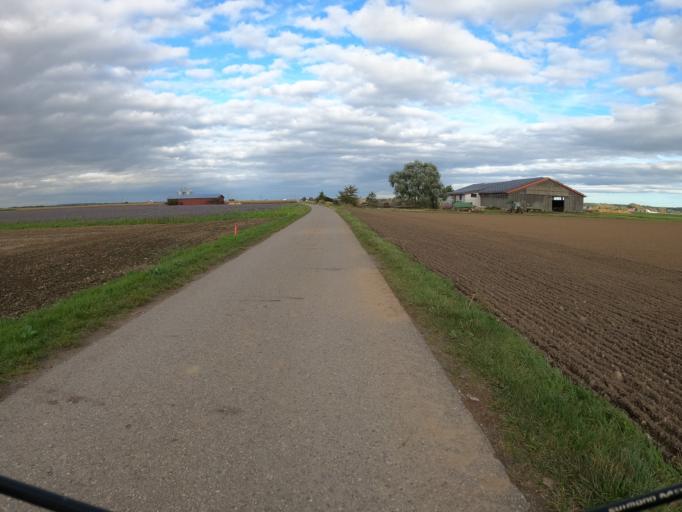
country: DE
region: Bavaria
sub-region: Swabia
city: Holzheim
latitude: 48.4018
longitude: 10.1077
